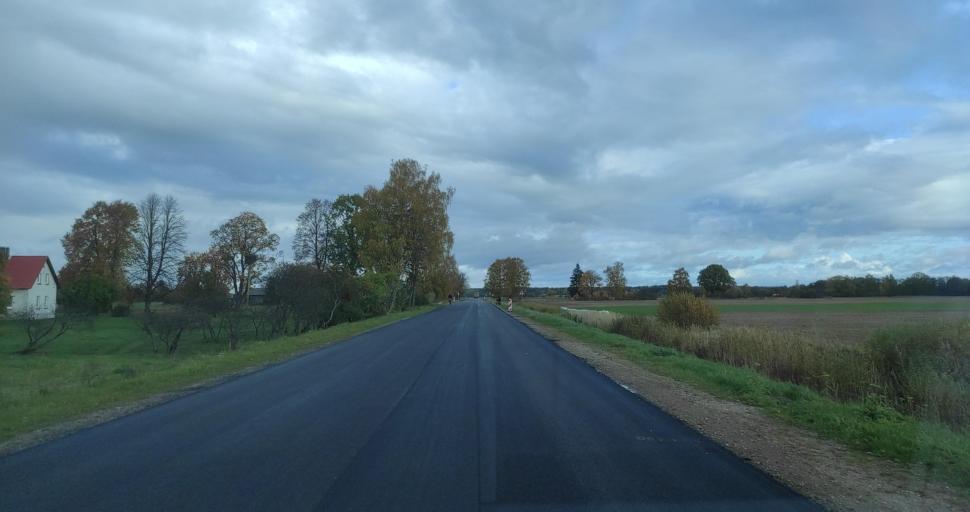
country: LV
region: Skrunda
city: Skrunda
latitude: 56.6869
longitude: 22.0190
